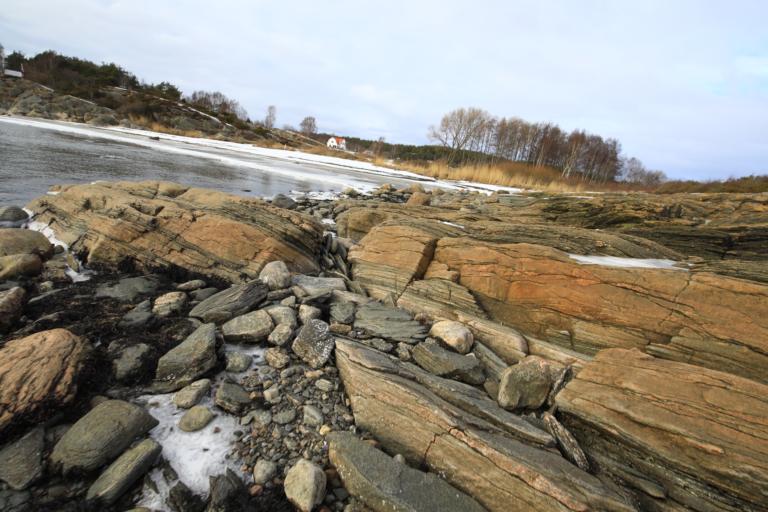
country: SE
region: Halland
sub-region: Kungsbacka Kommun
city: Frillesas
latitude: 57.2152
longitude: 12.1557
